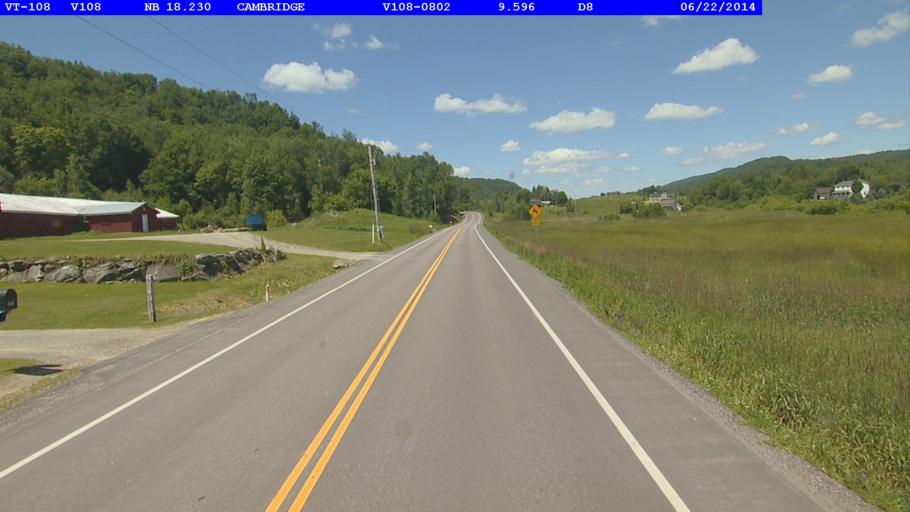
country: US
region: Vermont
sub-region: Lamoille County
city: Johnson
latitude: 44.6545
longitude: -72.8281
